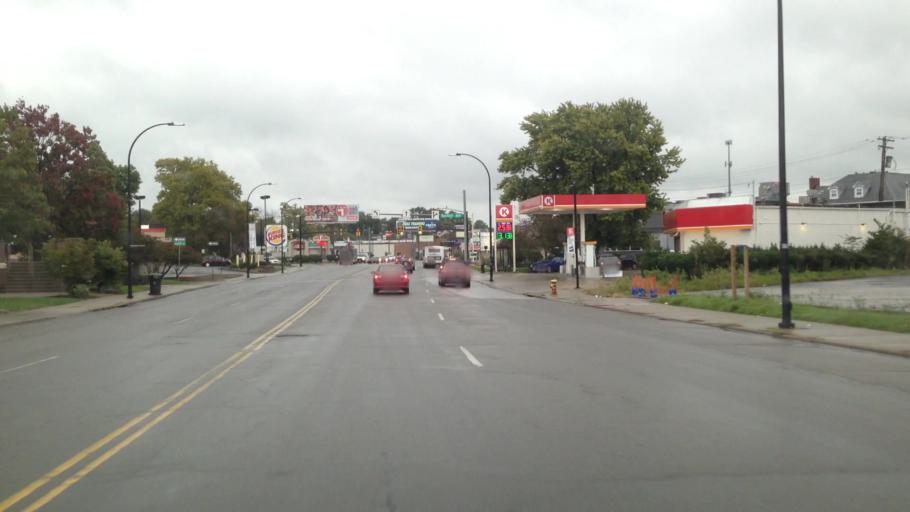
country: US
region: Ohio
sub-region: Summit County
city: Akron
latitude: 41.0774
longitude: -81.4978
